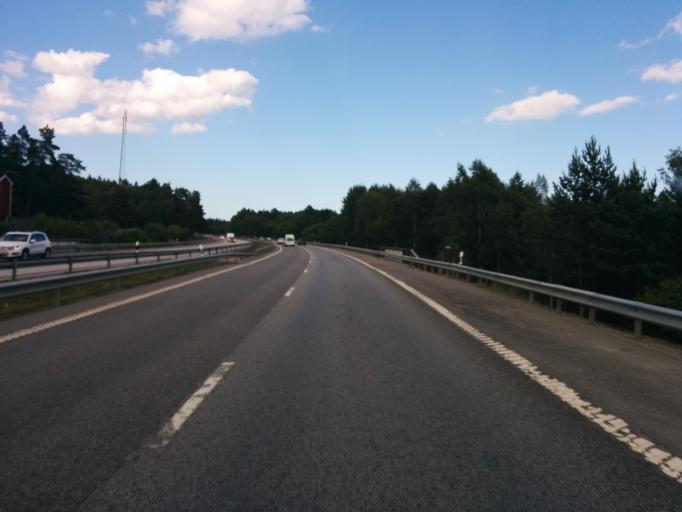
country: SE
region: Stockholm
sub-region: Nacka Kommun
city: Boo
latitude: 59.3178
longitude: 18.2798
